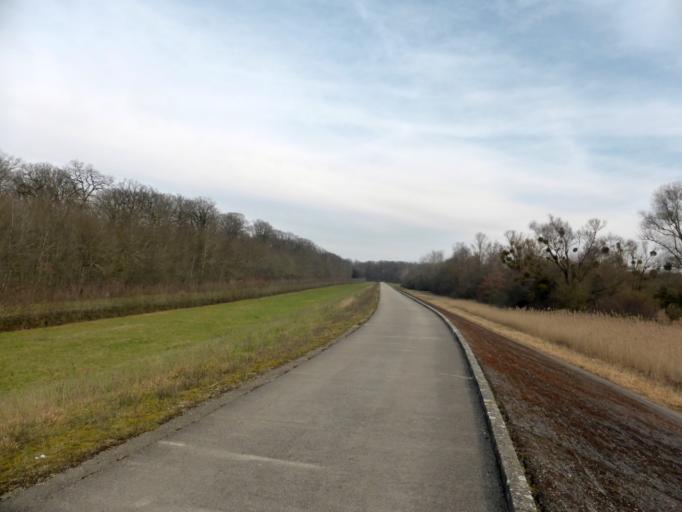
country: FR
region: Champagne-Ardenne
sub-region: Departement de l'Aube
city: Lusigny-sur-Barse
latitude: 48.2786
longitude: 4.3064
